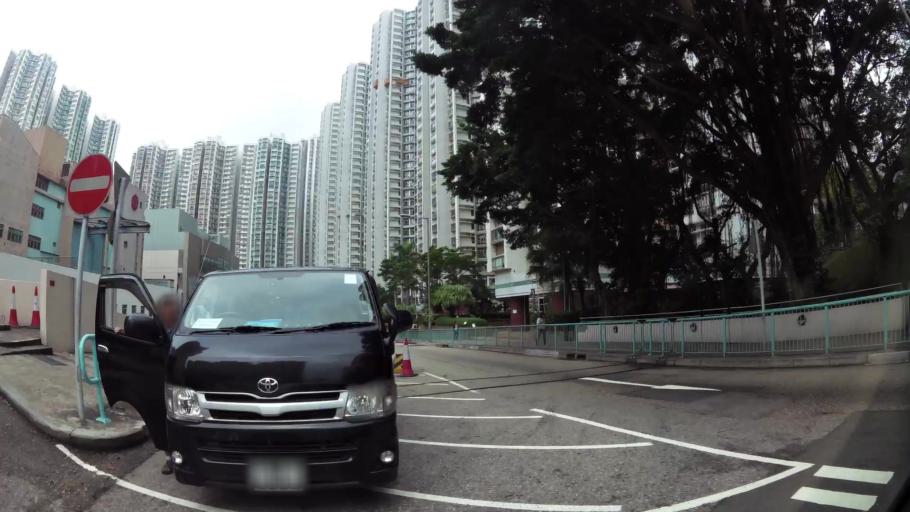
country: HK
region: Central and Western
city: Central
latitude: 22.2443
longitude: 114.1482
